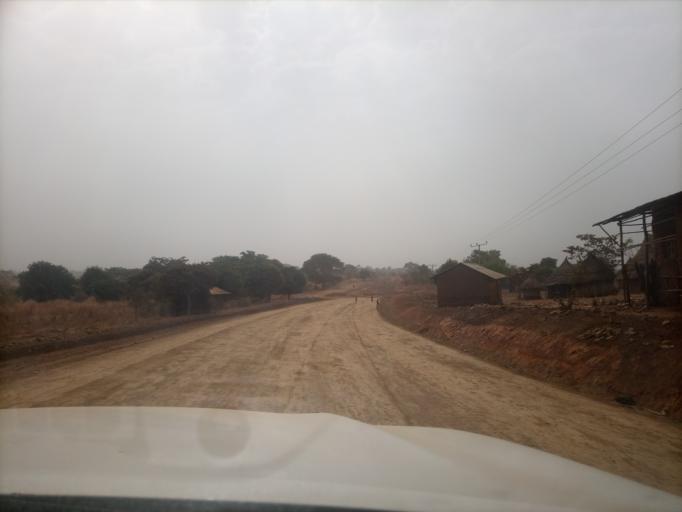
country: ET
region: Oromiya
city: Mendi
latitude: 10.1325
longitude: 35.1270
